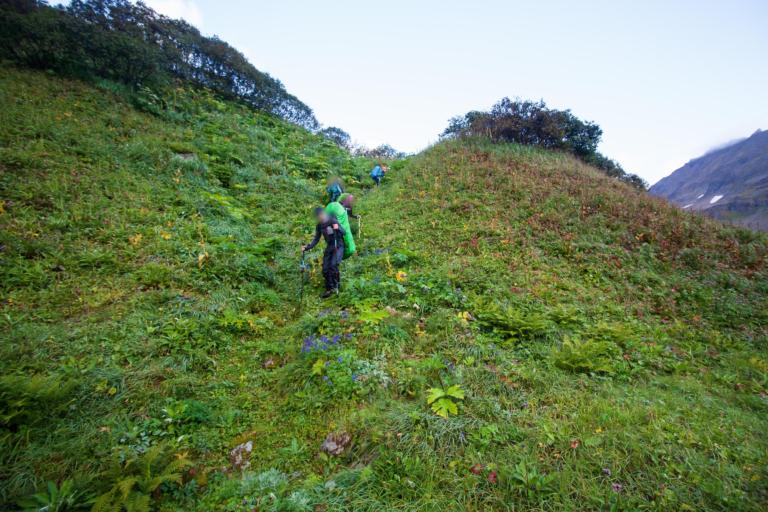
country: RU
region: Kamtsjatka
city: Yelizovo
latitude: 53.8578
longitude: 158.2654
